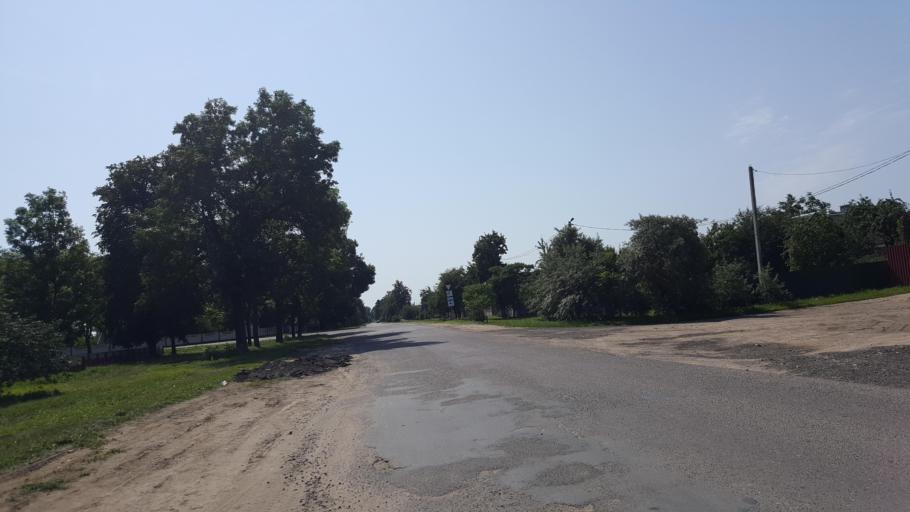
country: BY
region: Brest
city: Zhabinka
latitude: 52.2033
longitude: 24.0065
